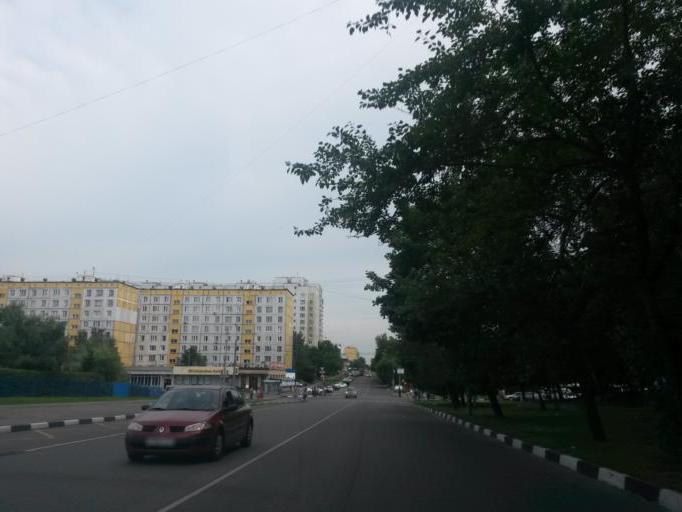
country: RU
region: Moscow
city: Orekhovo-Borisovo
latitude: 55.6110
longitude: 37.7314
